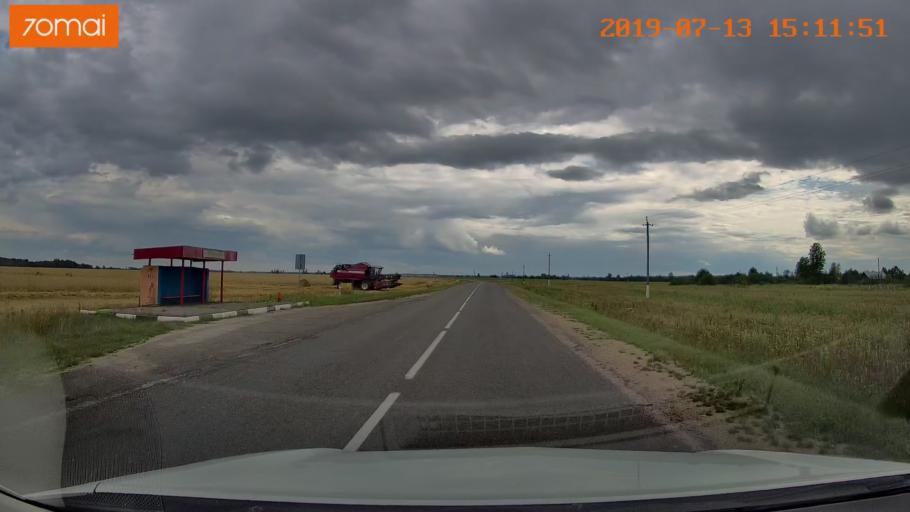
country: BY
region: Mogilev
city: Hlusha
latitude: 53.1561
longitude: 28.7872
